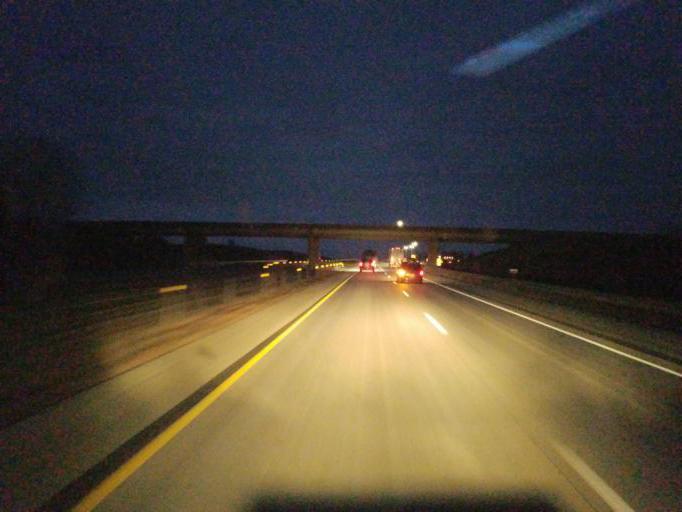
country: US
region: Iowa
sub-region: Guthrie County
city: Guthrie Center
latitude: 41.4967
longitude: -94.5679
